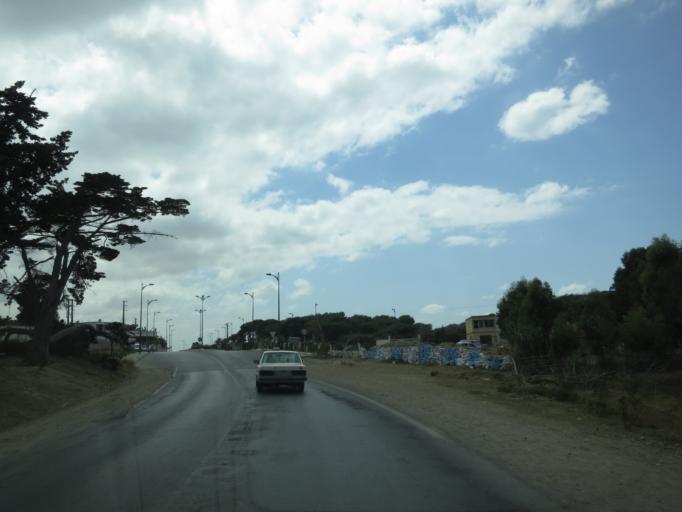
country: MA
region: Tanger-Tetouan
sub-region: Tanger-Assilah
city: Tangier
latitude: 35.8118
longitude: -5.7383
